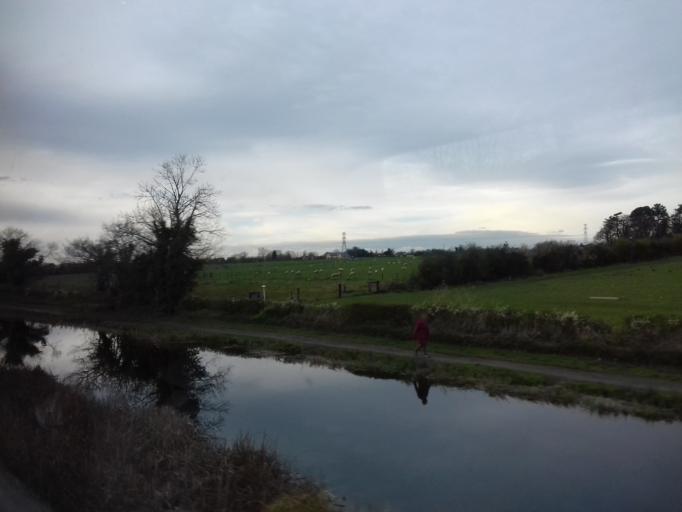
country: IE
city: Confey
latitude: 53.3753
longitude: -6.4946
